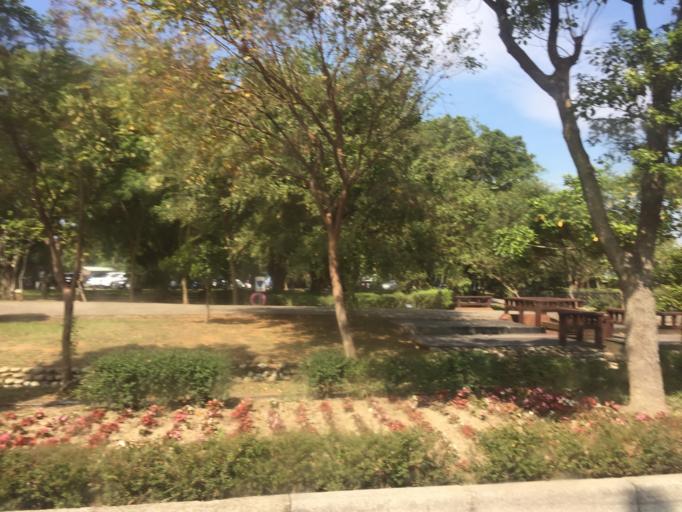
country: TW
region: Taiwan
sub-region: Taoyuan
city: Taoyuan
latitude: 24.9413
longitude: 121.3115
